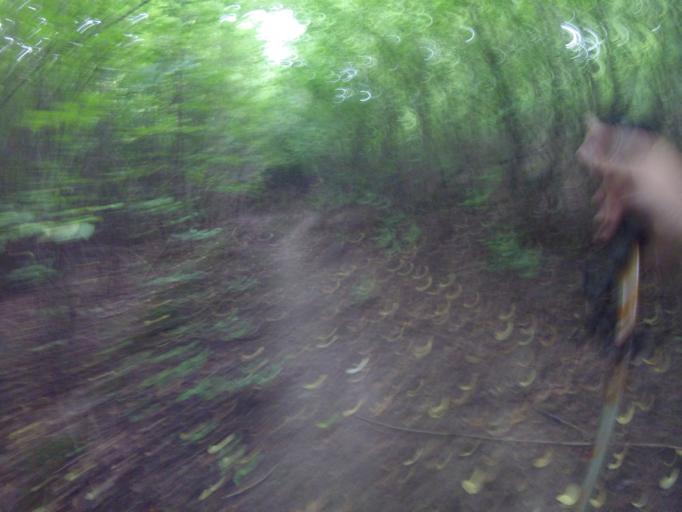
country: SK
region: Nitriansky
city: Sahy
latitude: 48.0418
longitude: 18.9779
